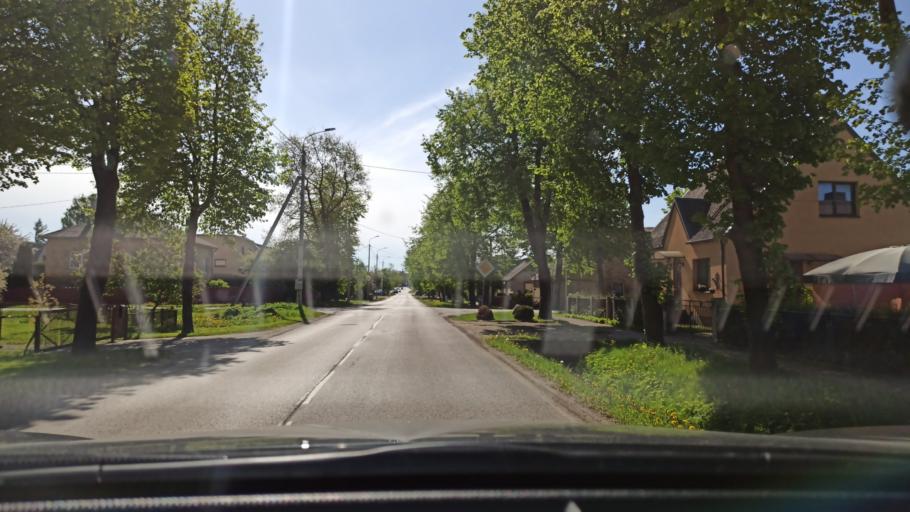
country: LT
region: Siauliu apskritis
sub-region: Siauliai
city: Siauliai
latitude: 55.9536
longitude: 23.2981
